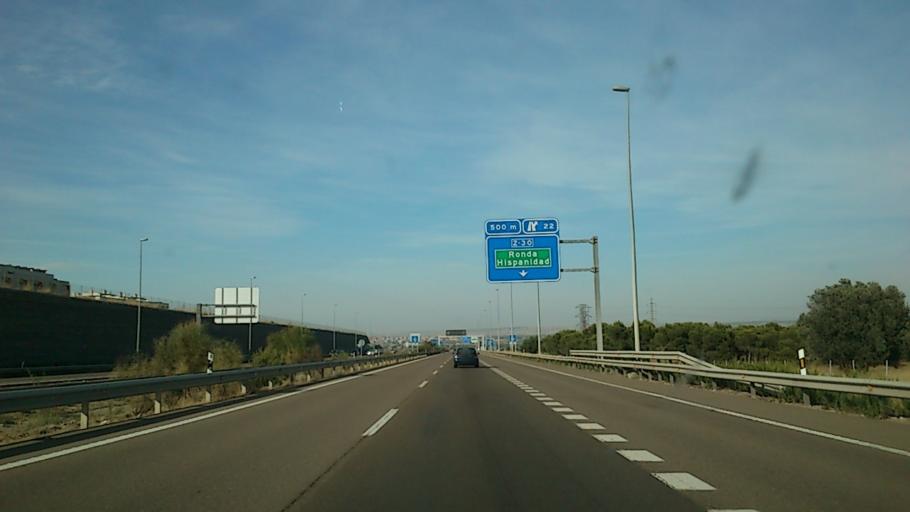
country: ES
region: Aragon
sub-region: Provincia de Zaragoza
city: Zaragoza
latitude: 41.6134
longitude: -0.8714
